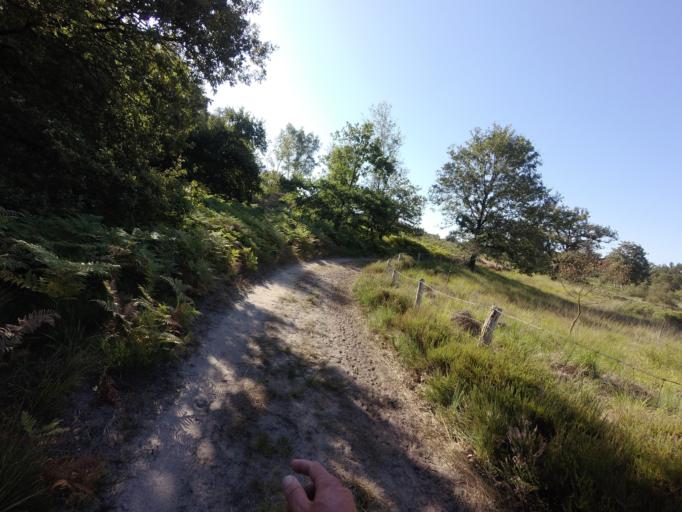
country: NL
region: Limburg
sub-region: Gemeente Roerdalen
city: Vlodrop
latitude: 51.1813
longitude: 6.1327
